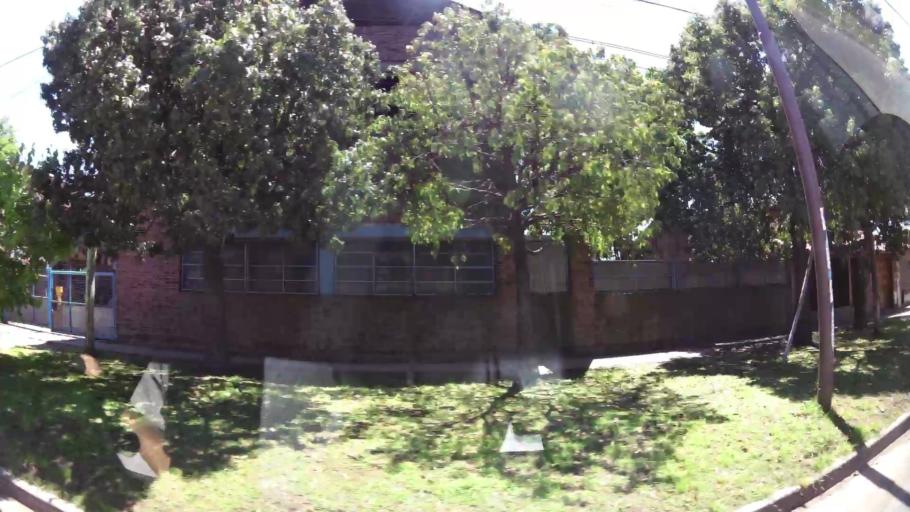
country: AR
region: Buenos Aires
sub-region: Partido de Quilmes
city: Quilmes
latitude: -34.7365
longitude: -58.2965
